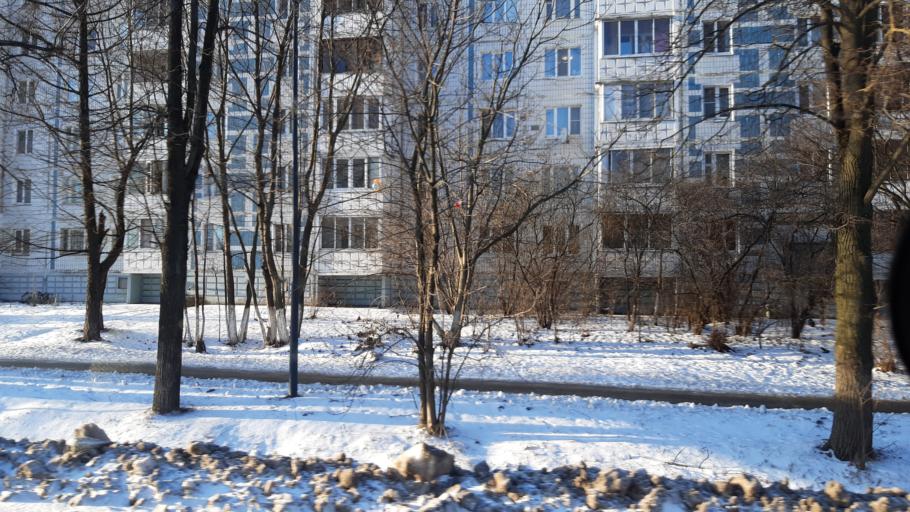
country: RU
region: Moskovskaya
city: Sergiyev Posad
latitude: 56.3279
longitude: 38.1508
